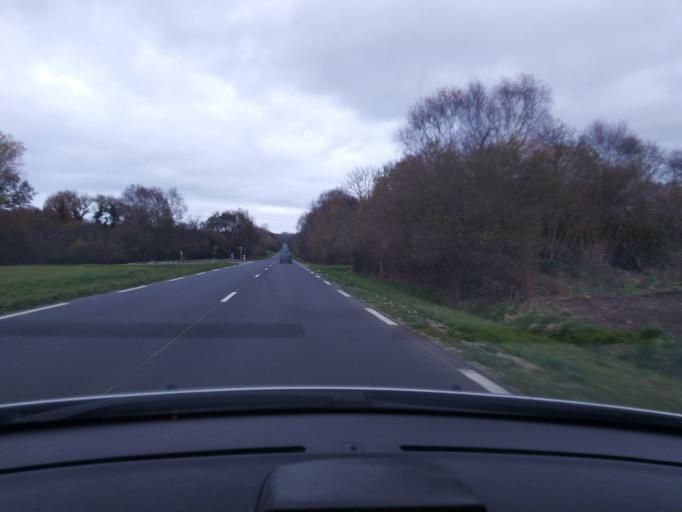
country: FR
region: Brittany
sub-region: Departement des Cotes-d'Armor
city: Plounevez-Moedec
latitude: 48.5711
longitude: -3.4951
